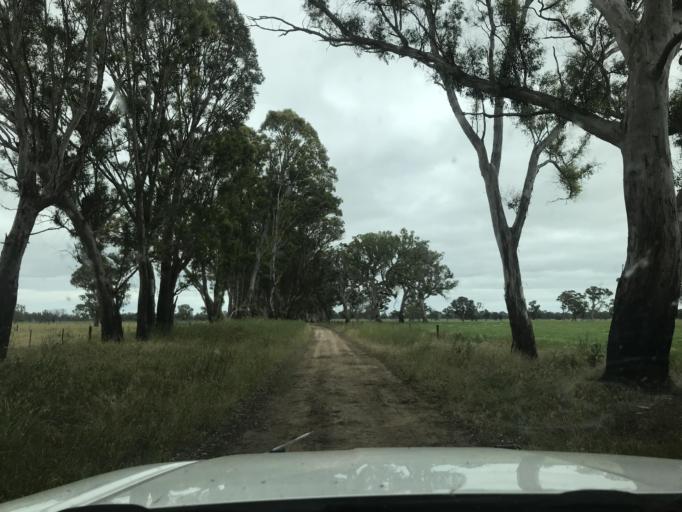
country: AU
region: South Australia
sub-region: Wattle Range
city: Penola
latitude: -37.1788
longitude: 141.0561
